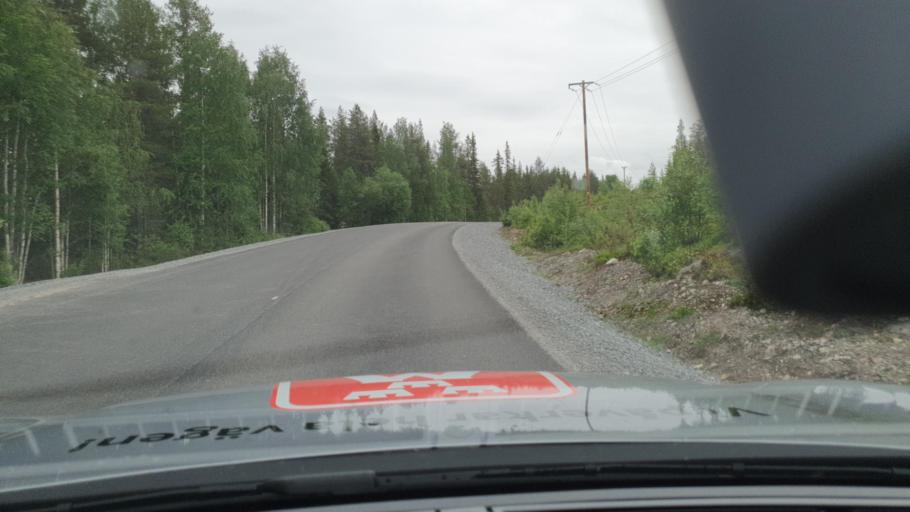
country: SE
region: Norrbotten
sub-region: Overtornea Kommun
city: OEvertornea
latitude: 66.6240
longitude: 23.2826
